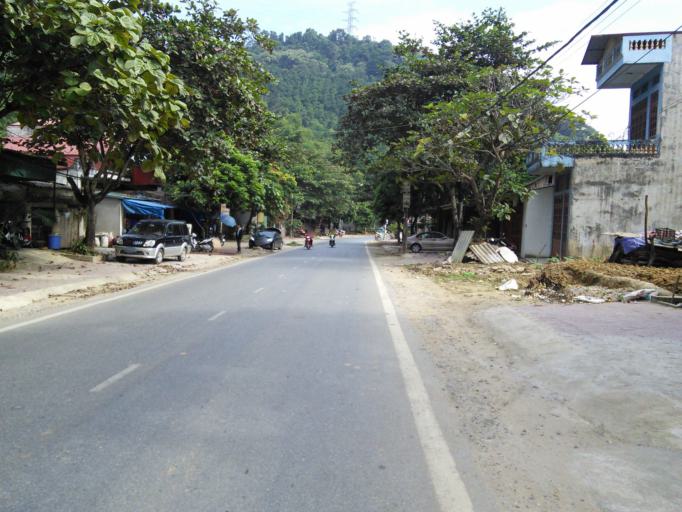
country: VN
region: Lao Cai
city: Lao Cai
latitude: 22.4644
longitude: 103.9460
